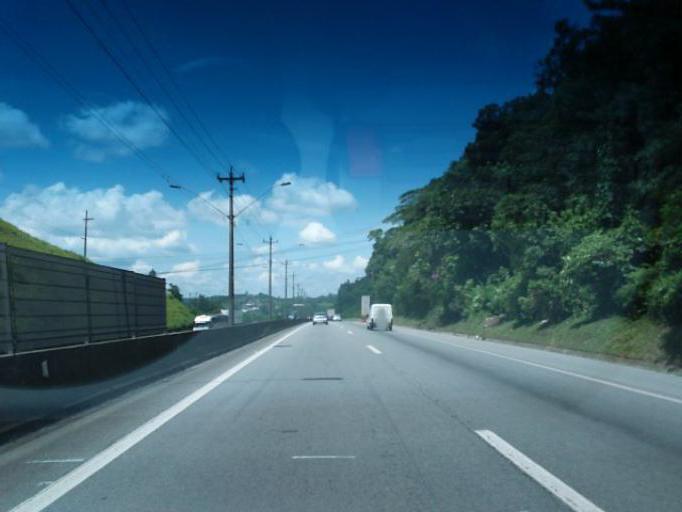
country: BR
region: Sao Paulo
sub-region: Sao Lourenco Da Serra
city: Sao Lourenco da Serra
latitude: -23.8865
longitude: -46.9773
